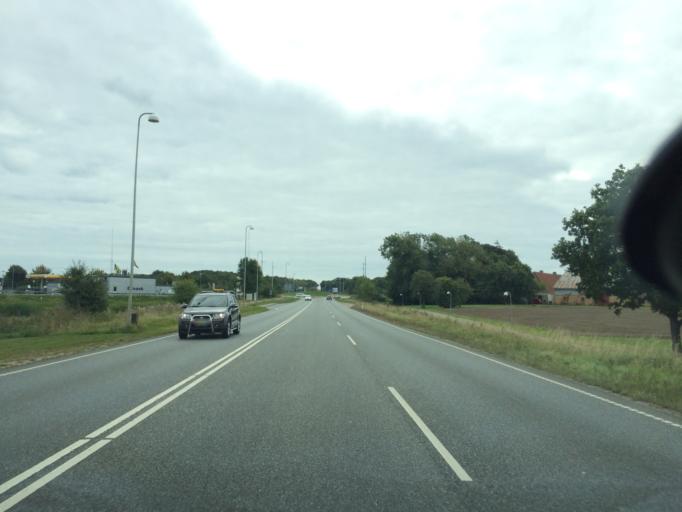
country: DK
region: South Denmark
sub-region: Aabenraa Kommune
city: Rodekro
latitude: 55.0685
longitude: 9.3585
